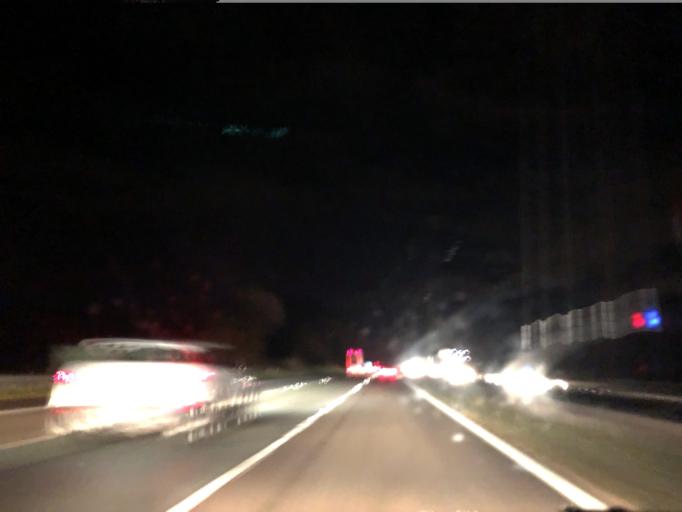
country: GB
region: England
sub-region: Staffordshire
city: Newcastle under Lyme
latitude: 52.9893
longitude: -2.2619
